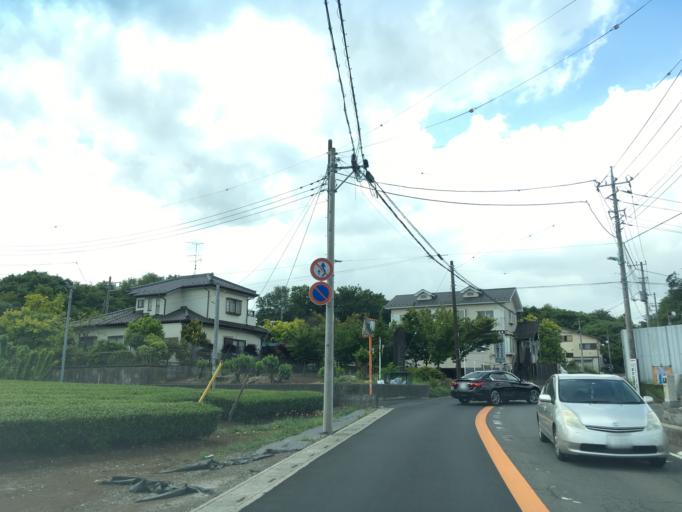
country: JP
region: Saitama
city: Tokorozawa
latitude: 35.7862
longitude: 139.4167
